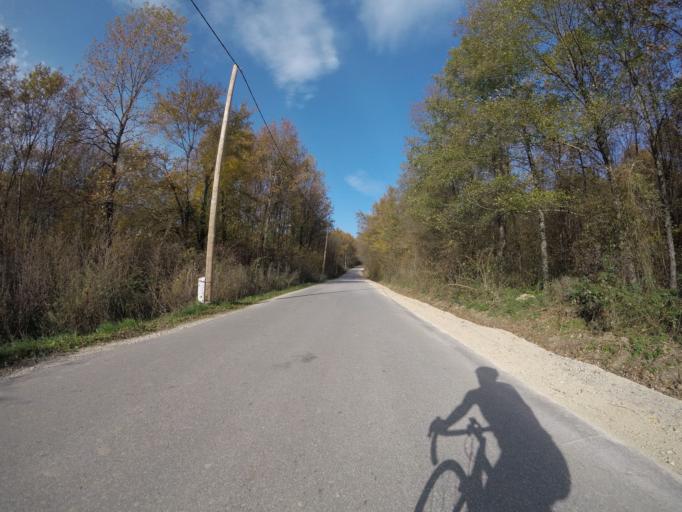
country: HR
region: Zagrebacka
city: Gradici
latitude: 45.6299
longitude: 16.0226
